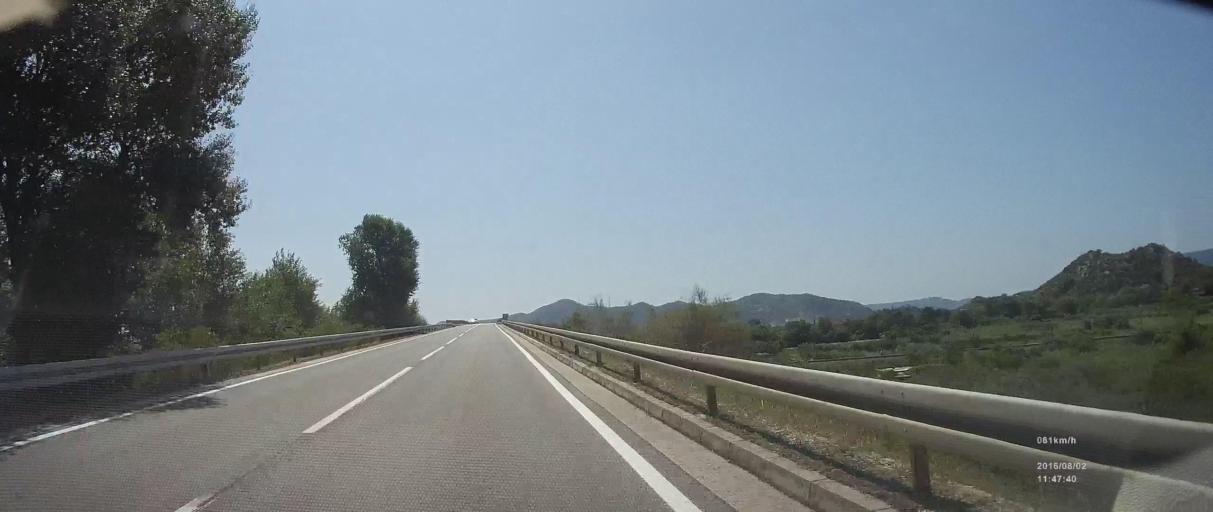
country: HR
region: Dubrovacko-Neretvanska
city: Komin
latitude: 43.0414
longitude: 17.4834
